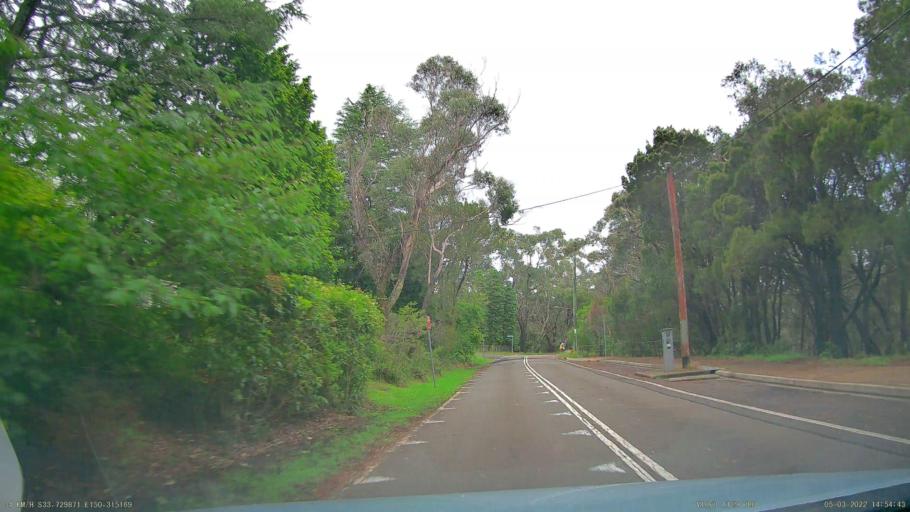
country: AU
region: New South Wales
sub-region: Blue Mountains Municipality
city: Katoomba
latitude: -33.7297
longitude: 150.3152
